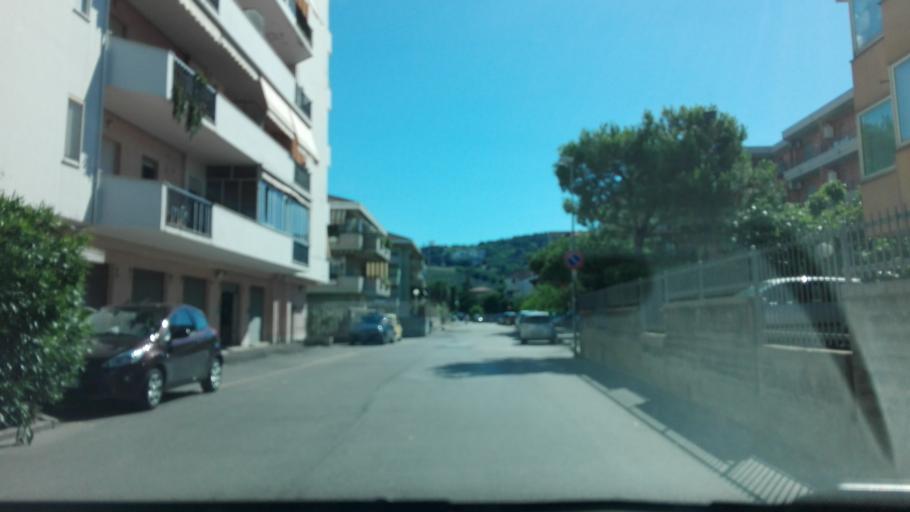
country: IT
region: Abruzzo
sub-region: Provincia di Pescara
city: Montesilvano Marina
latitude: 42.5055
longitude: 14.1715
